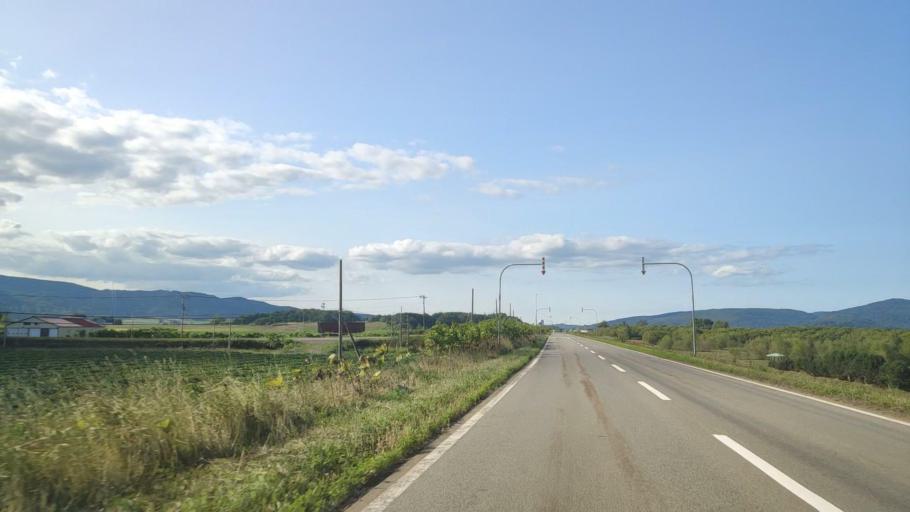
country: JP
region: Hokkaido
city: Nayoro
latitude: 44.8060
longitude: 142.0671
